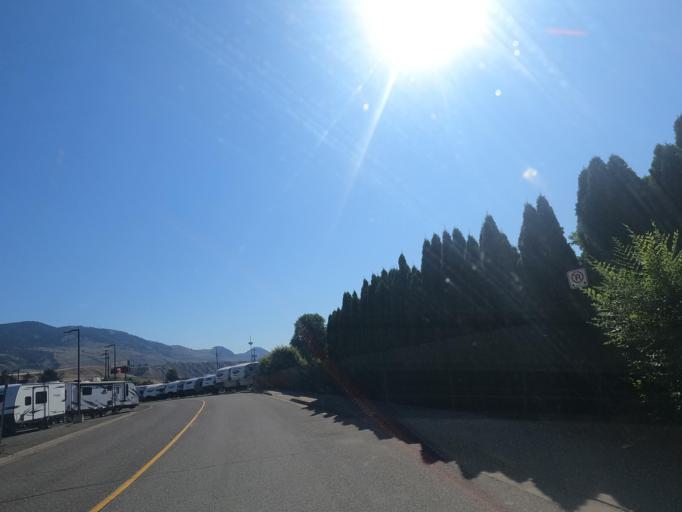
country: CA
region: British Columbia
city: Kamloops
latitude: 50.6761
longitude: -120.2511
